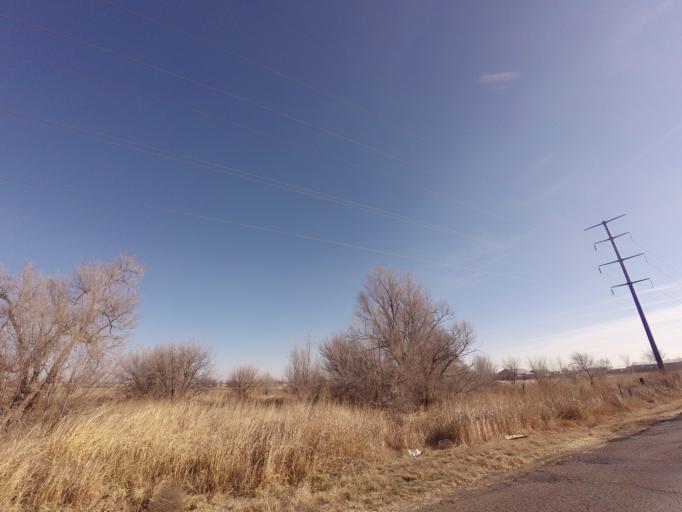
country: US
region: New Mexico
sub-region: Curry County
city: Clovis
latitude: 34.4159
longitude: -103.2493
